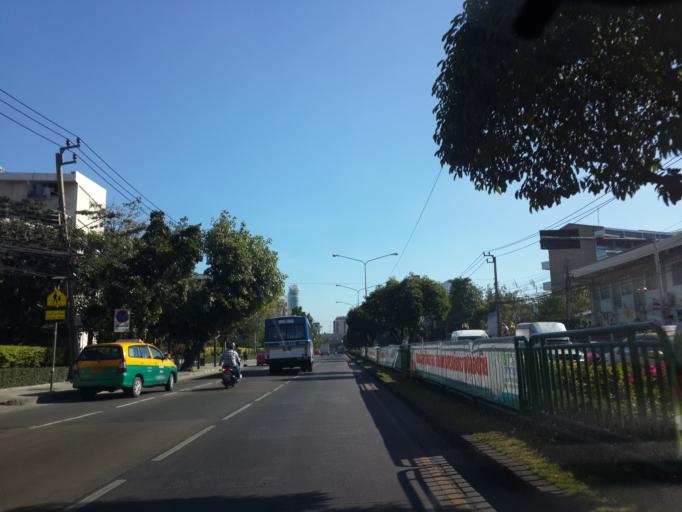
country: TH
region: Bangkok
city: Bang Kapi
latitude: 13.7720
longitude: 100.6472
